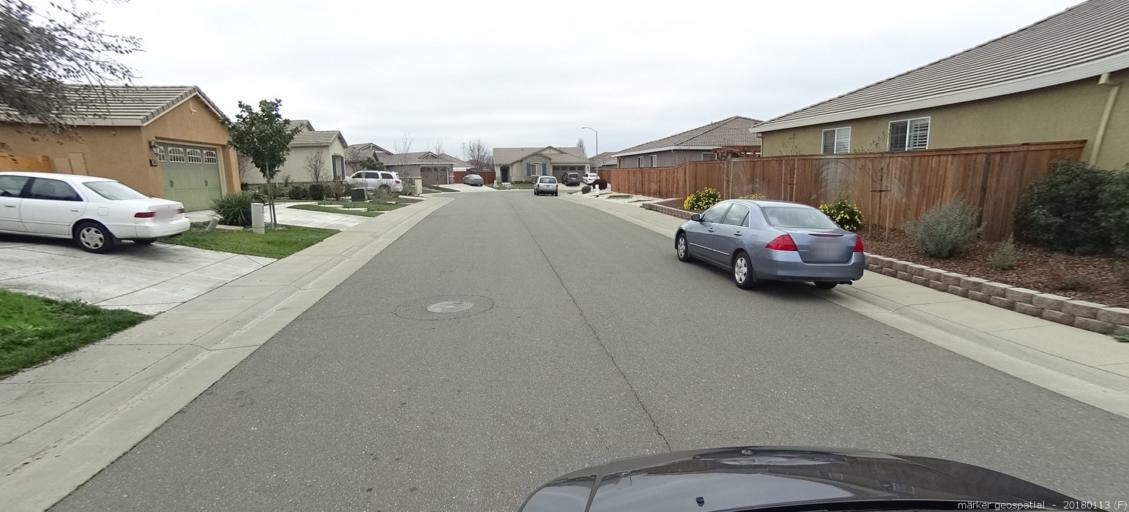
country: US
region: California
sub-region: Sacramento County
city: Gold River
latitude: 38.5586
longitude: -121.2110
